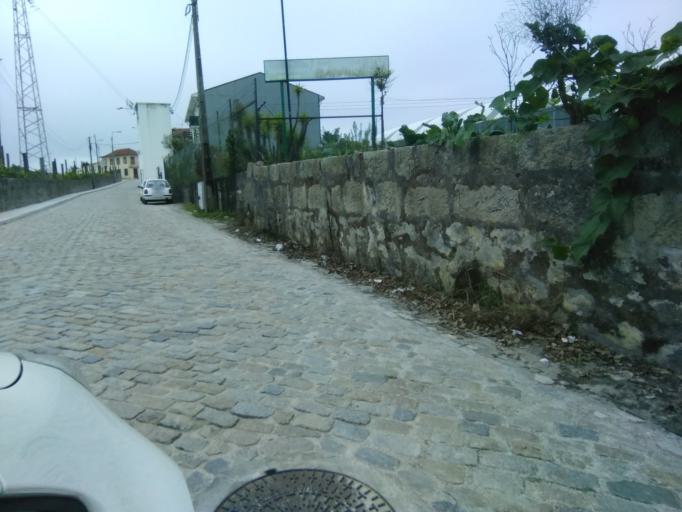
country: PT
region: Porto
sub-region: Matosinhos
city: Santa Cruz do Bispo
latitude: 41.2260
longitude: -8.7044
